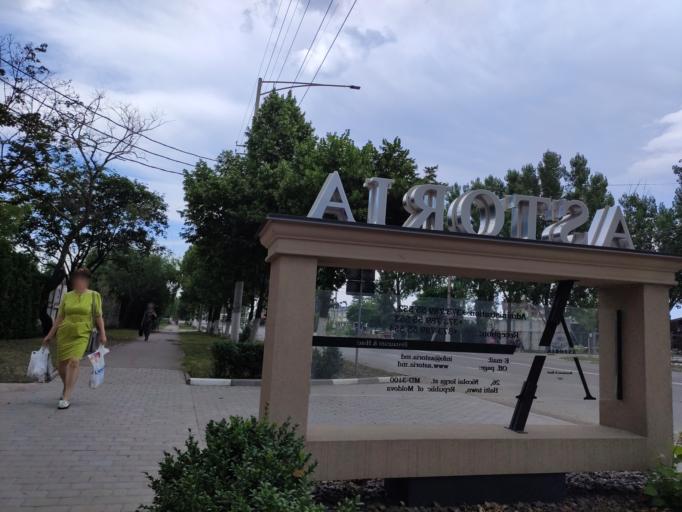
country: MD
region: Balti
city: Balti
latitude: 47.7603
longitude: 27.9408
